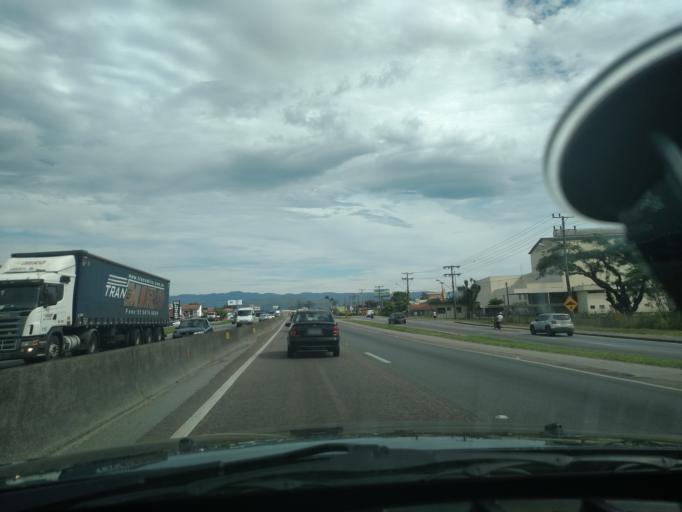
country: BR
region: Santa Catarina
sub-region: Biguacu
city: Biguacu
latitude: -27.5033
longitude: -48.6515
